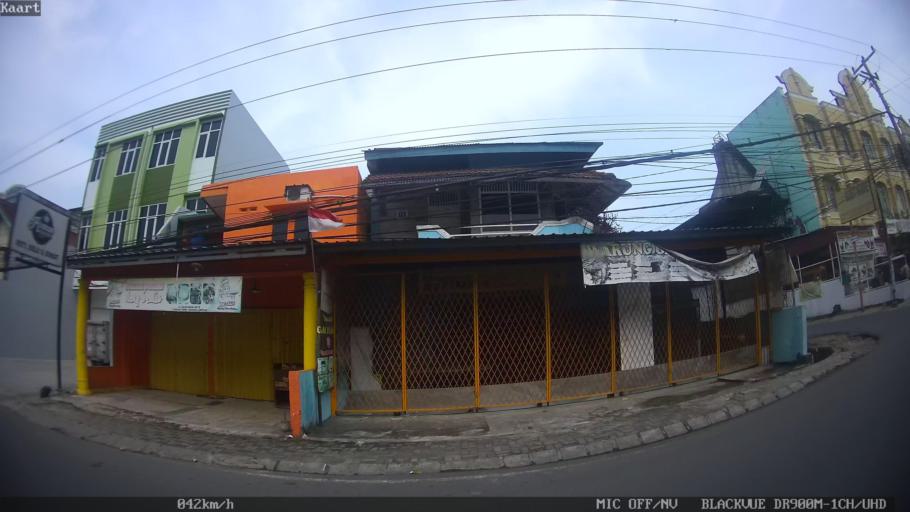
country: ID
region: Lampung
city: Bandarlampung
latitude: -5.4135
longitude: 105.2672
